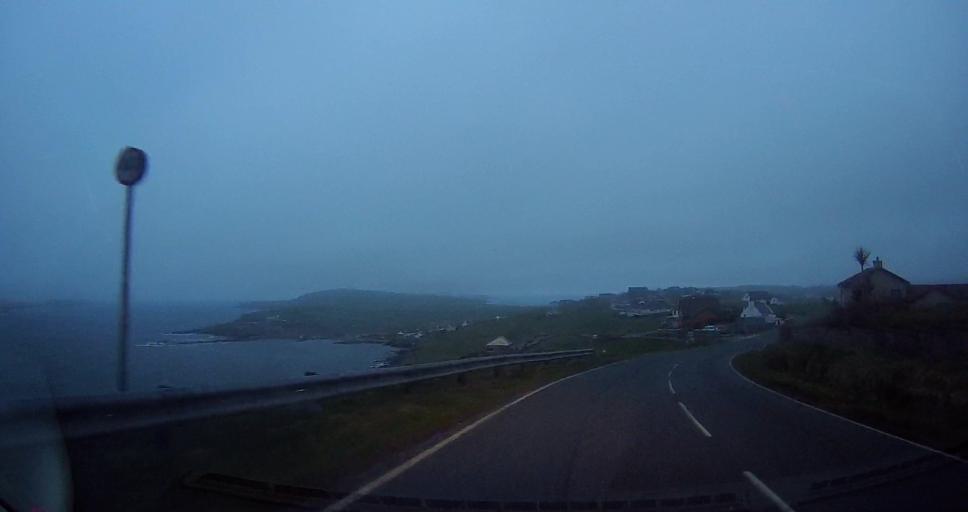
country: GB
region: Scotland
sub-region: Shetland Islands
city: Sandwick
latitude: 60.0129
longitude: -1.2261
